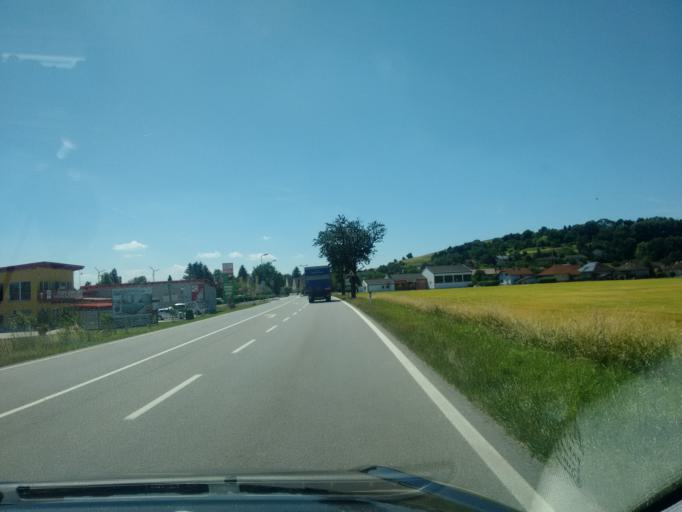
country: AT
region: Lower Austria
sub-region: Politischer Bezirk Sankt Polten
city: Haunoldstein
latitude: 48.1950
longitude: 15.4633
